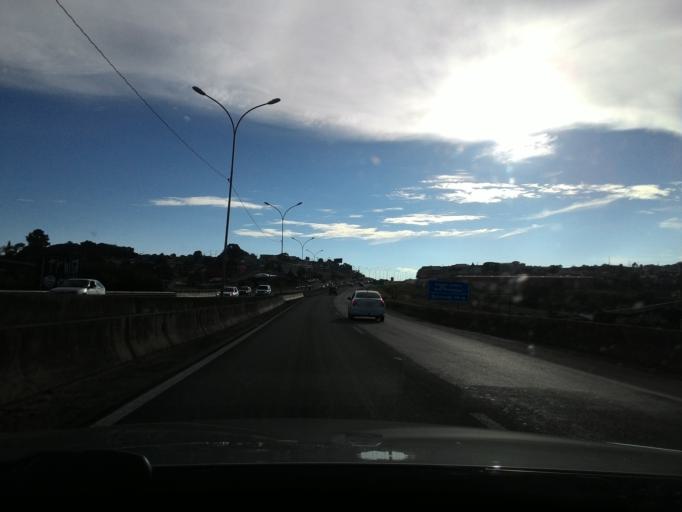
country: BR
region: Parana
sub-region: Pinhais
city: Pinhais
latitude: -25.3869
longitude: -49.1761
